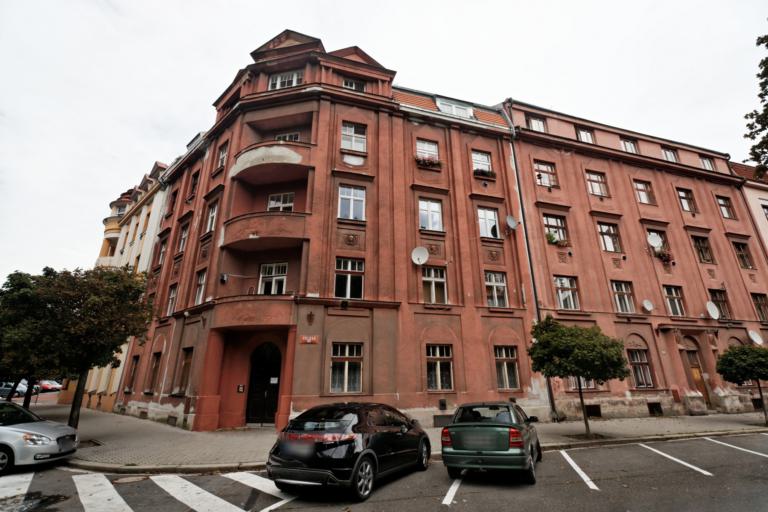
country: CZ
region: Pardubicky
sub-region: Okres Pardubice
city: Pardubice
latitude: 50.0376
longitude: 15.7839
